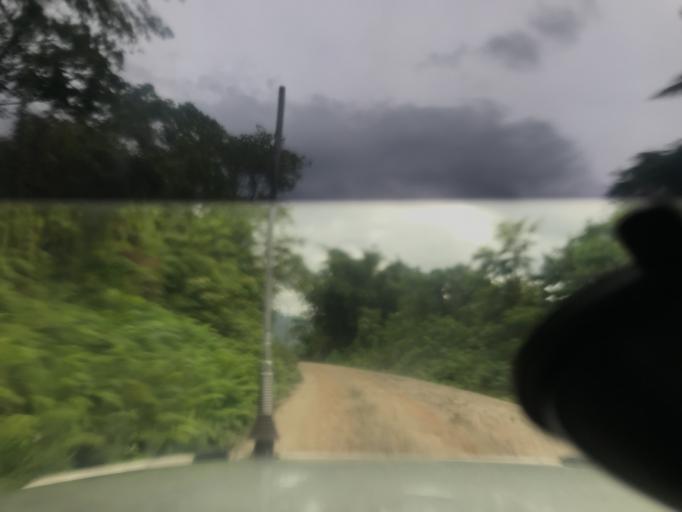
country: SB
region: Malaita
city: Auki
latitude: -8.8922
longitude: 160.7747
